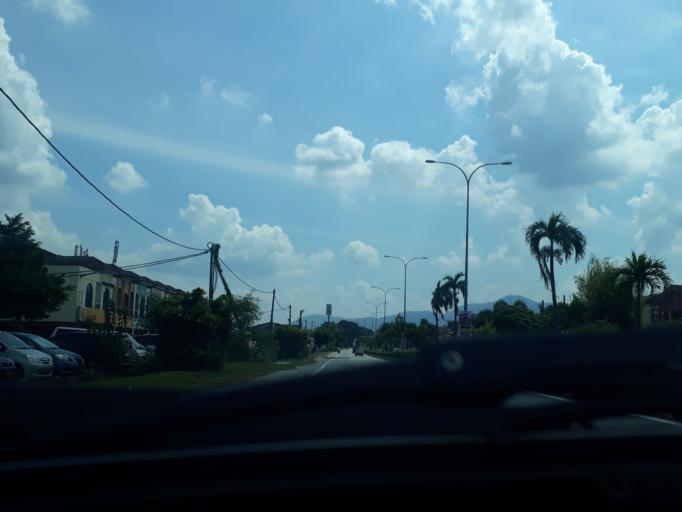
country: MY
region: Perak
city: Ipoh
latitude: 4.5774
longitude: 101.0970
